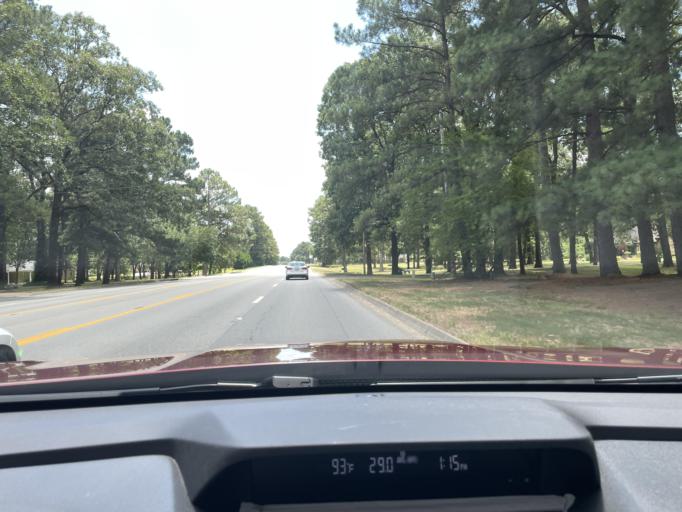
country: US
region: Arkansas
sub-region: Drew County
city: Monticello
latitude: 33.6553
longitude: -91.8027
